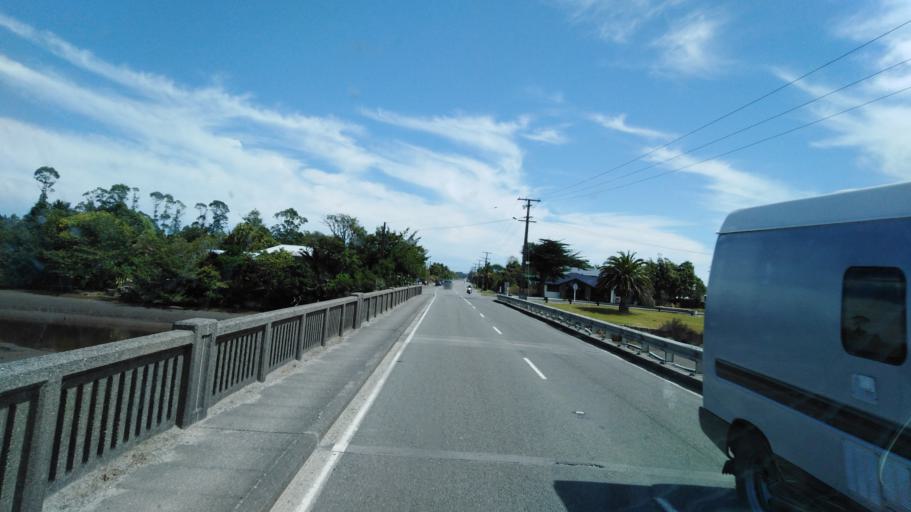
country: NZ
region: West Coast
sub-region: Buller District
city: Westport
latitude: -41.7521
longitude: 171.6250
